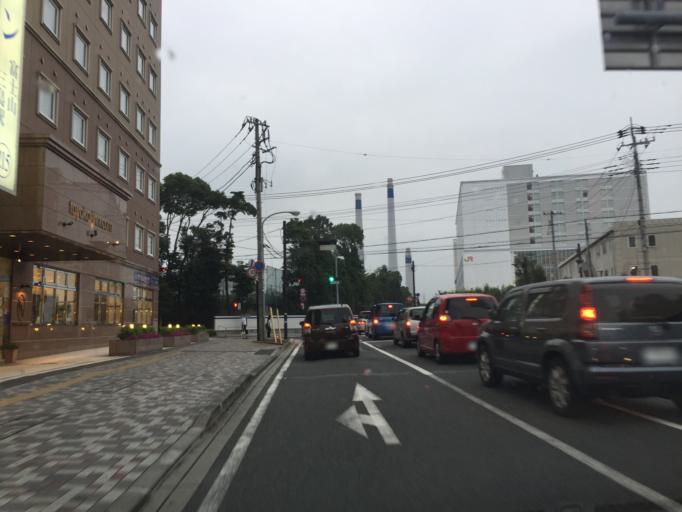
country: JP
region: Shizuoka
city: Mishima
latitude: 35.1283
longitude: 138.9107
